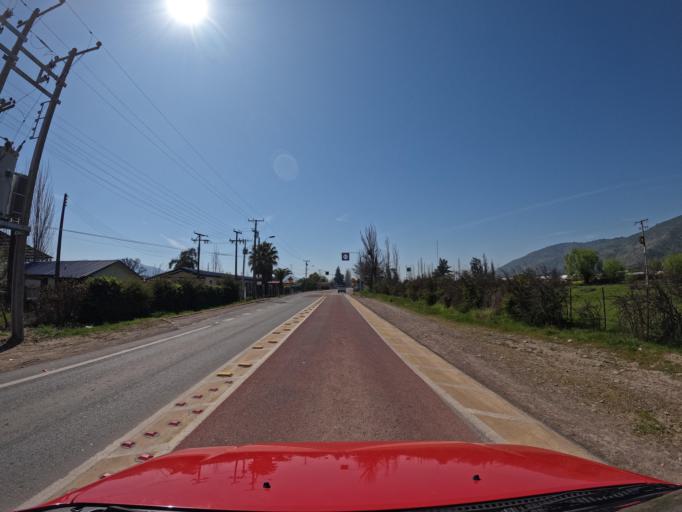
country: CL
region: Maule
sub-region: Provincia de Curico
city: Rauco
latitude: -35.0235
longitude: -71.4324
